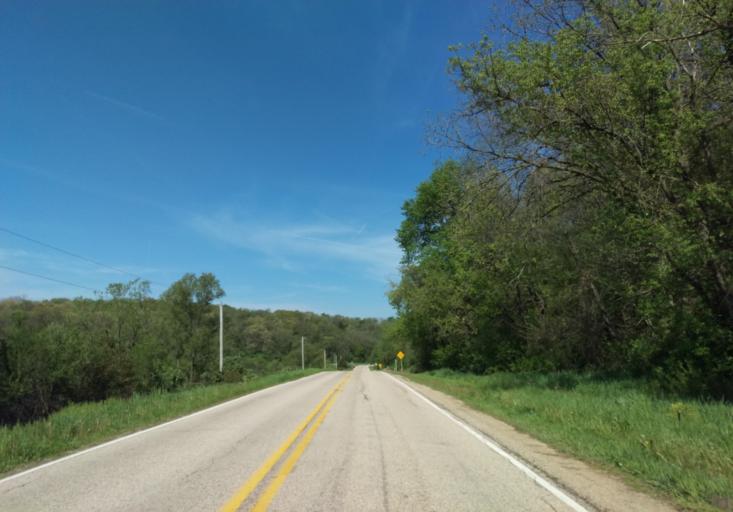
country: US
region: Wisconsin
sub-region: Dane County
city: Mount Horeb
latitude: 43.0588
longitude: -89.7791
